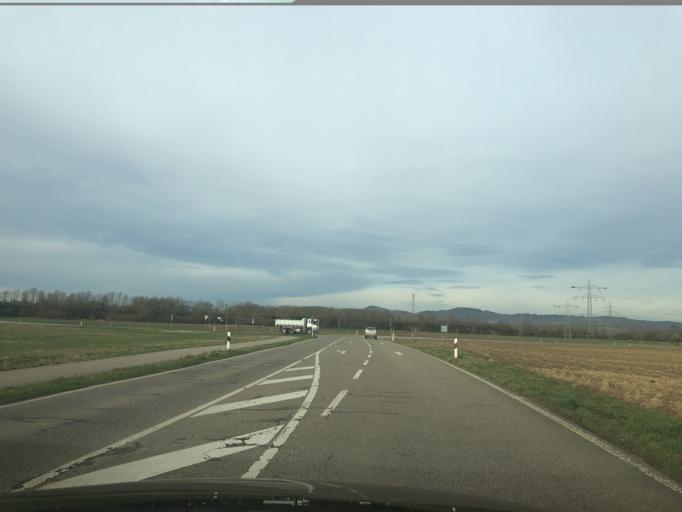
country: DE
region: Baden-Wuerttemberg
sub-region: Freiburg Region
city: Vorstetten
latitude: 48.0766
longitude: 7.8140
